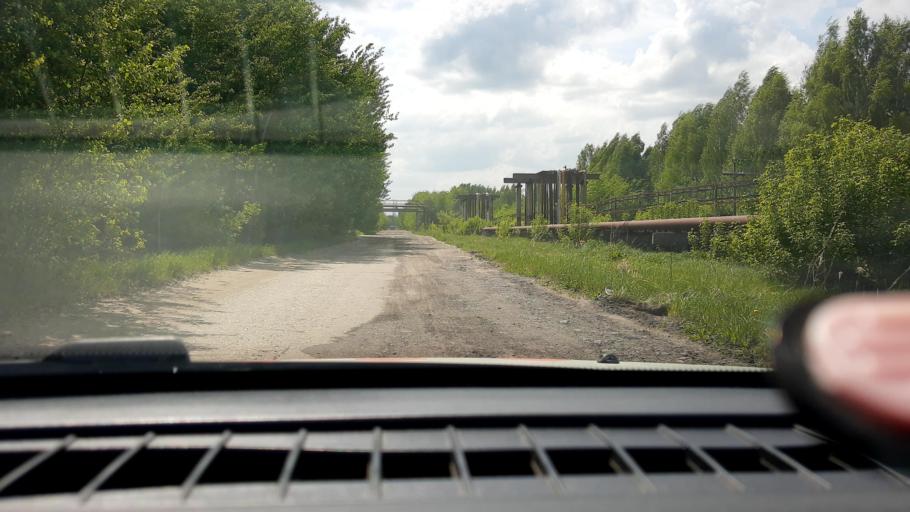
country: RU
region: Nizjnij Novgorod
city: Kstovo
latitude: 56.1298
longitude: 44.1280
